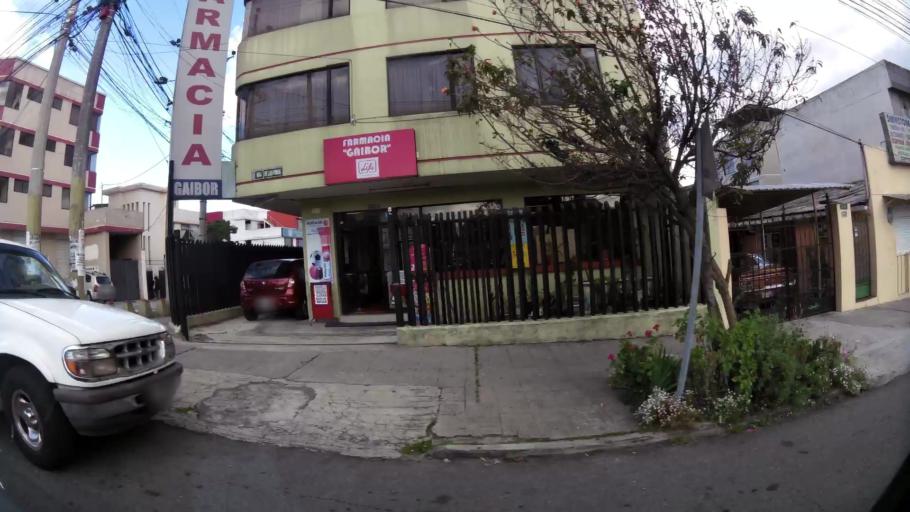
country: EC
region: Pichincha
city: Quito
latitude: -0.1374
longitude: -78.4765
